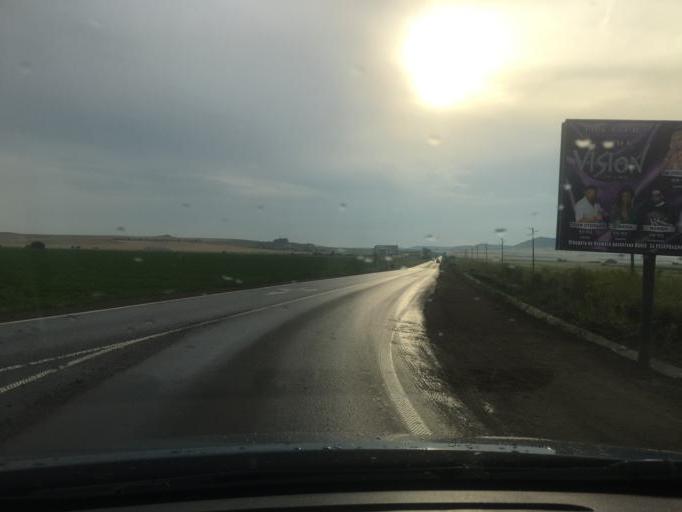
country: BG
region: Burgas
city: Aheloy
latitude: 42.6458
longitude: 27.6365
